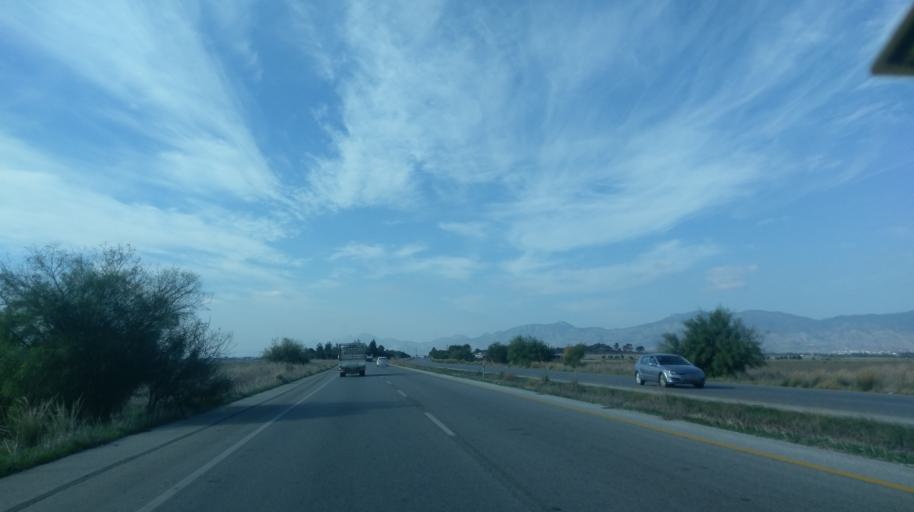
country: CY
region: Ammochostos
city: Lefkonoiko
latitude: 35.1916
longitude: 33.6246
